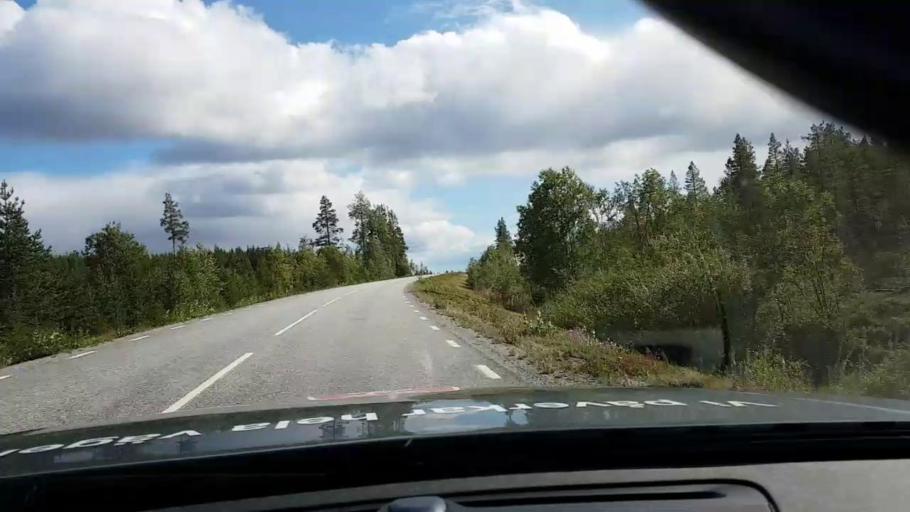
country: SE
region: Vaesterbotten
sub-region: Asele Kommun
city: Asele
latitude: 63.7724
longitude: 17.6784
